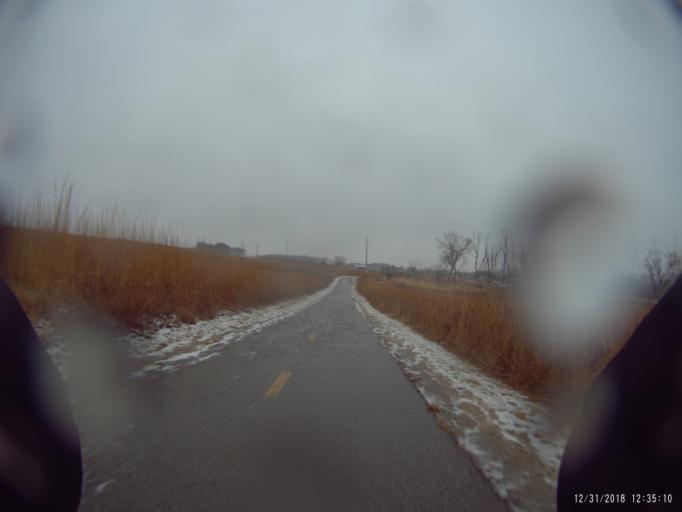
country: US
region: Wisconsin
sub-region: Dane County
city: Verona
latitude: 43.0140
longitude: -89.5180
